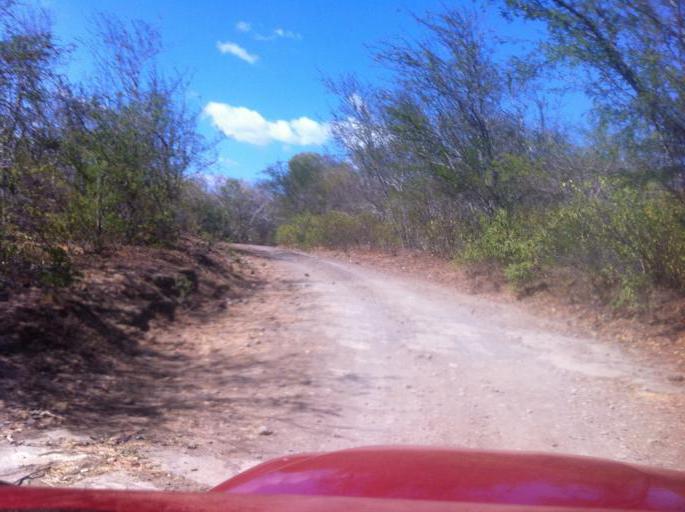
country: NI
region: Carazo
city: Santa Teresa
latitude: 11.6154
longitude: -86.3202
